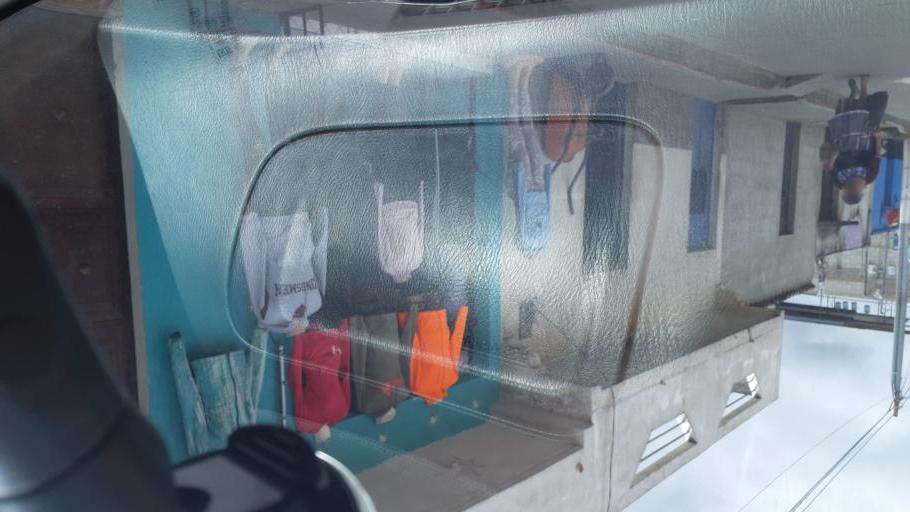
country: GT
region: Chimaltenango
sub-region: Municipio de Chimaltenango
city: Chimaltenango
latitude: 14.6638
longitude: -90.8181
